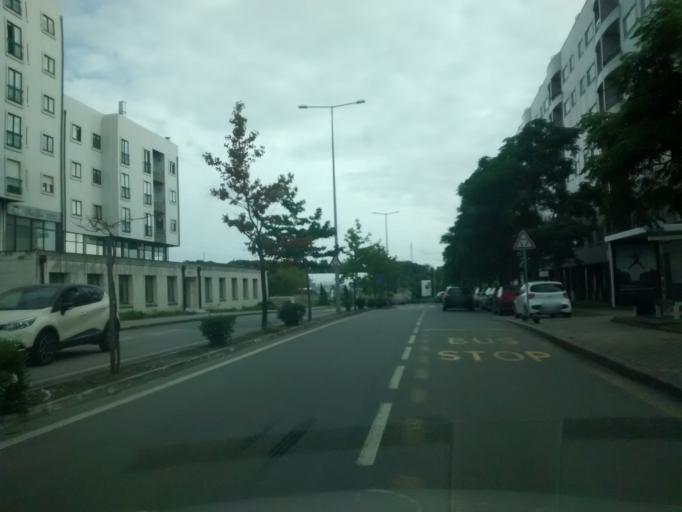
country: PT
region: Aveiro
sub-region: Aveiro
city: Aveiro
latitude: 40.6402
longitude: -8.6405
